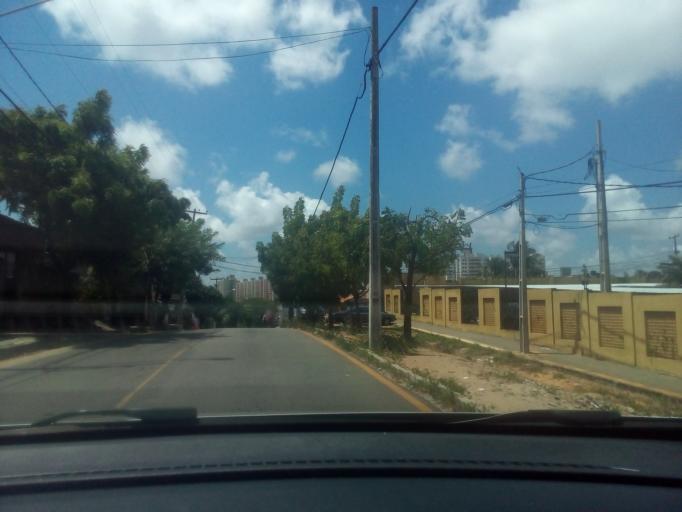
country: BR
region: Rio Grande do Norte
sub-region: Parnamirim
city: Parnamirim
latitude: -5.8711
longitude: -35.2117
